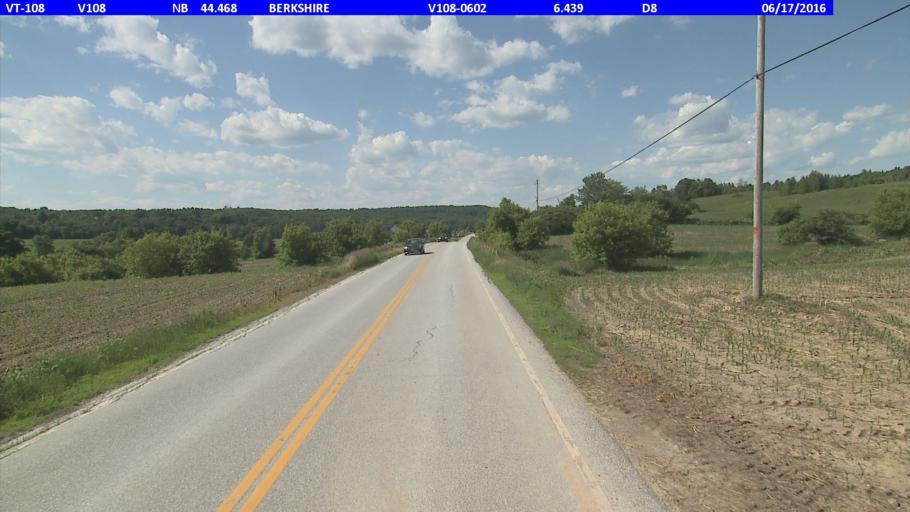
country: US
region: Vermont
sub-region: Franklin County
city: Enosburg Falls
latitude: 45.0097
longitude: -72.8245
